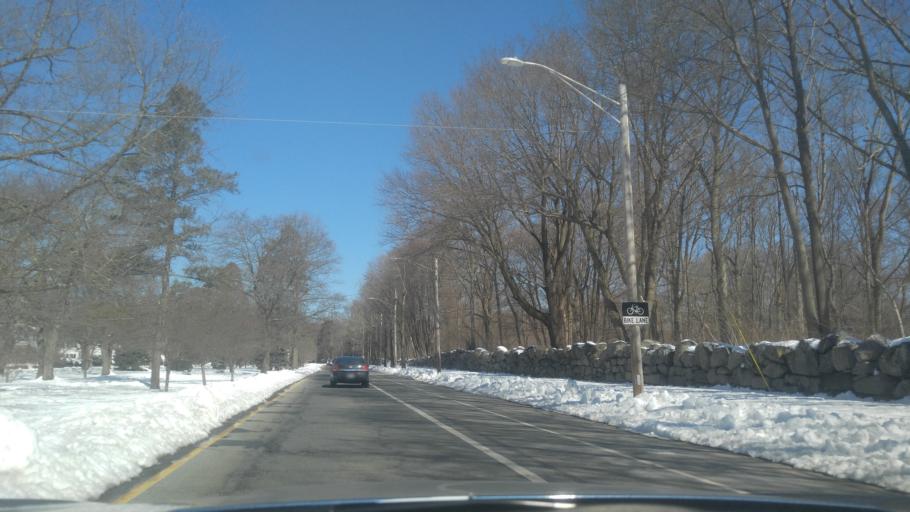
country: US
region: Rhode Island
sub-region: Providence County
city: Pawtucket
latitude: 41.8486
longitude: -71.3868
